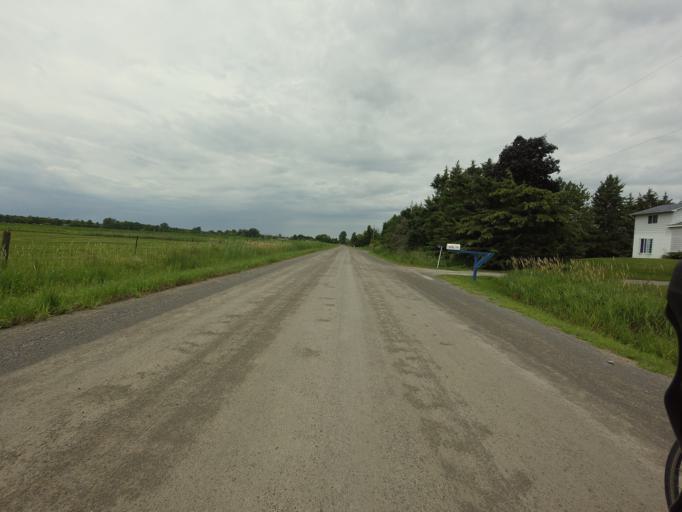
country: CA
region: Ontario
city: Bells Corners
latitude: 45.0747
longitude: -75.6047
